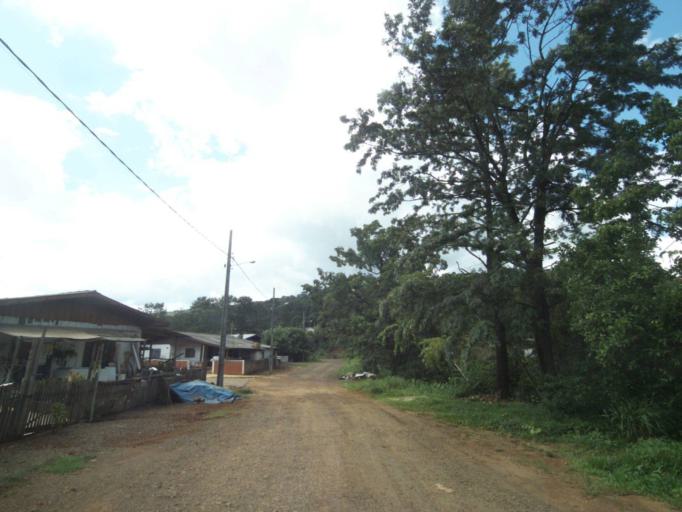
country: BR
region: Parana
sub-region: Uniao Da Vitoria
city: Uniao da Vitoria
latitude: -26.1501
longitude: -51.5422
